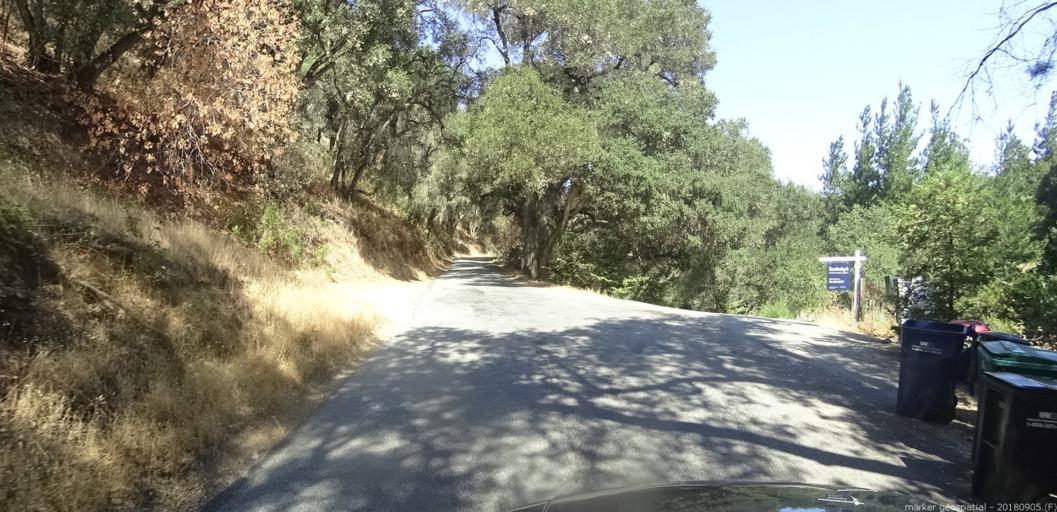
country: US
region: California
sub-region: Monterey County
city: Carmel Valley Village
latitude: 36.4149
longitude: -121.6755
